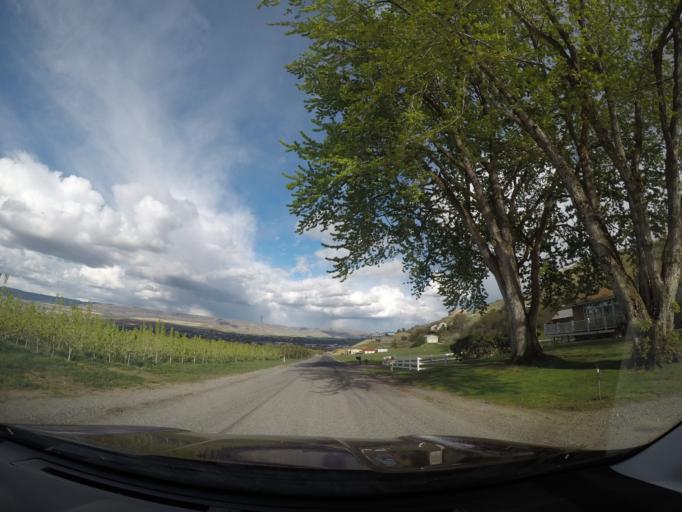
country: US
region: Washington
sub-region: Chelan County
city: Wenatchee
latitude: 47.3971
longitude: -120.3233
